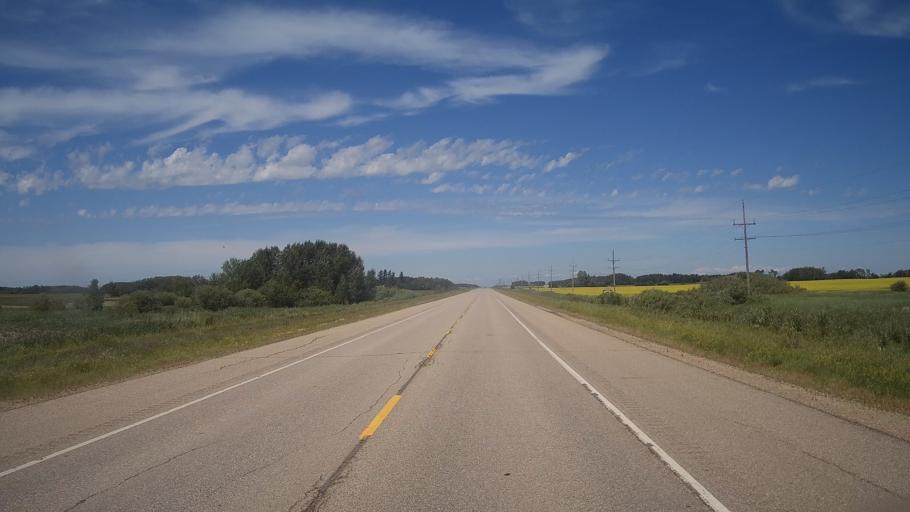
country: CA
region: Saskatchewan
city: Langenburg
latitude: 50.6539
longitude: -101.2760
